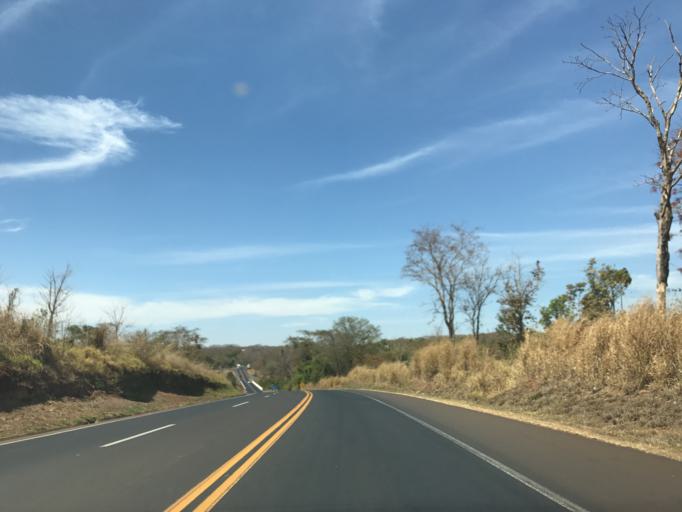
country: BR
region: Minas Gerais
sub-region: Monte Alegre De Minas
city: Monte Alegre de Minas
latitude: -19.0356
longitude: -49.0120
